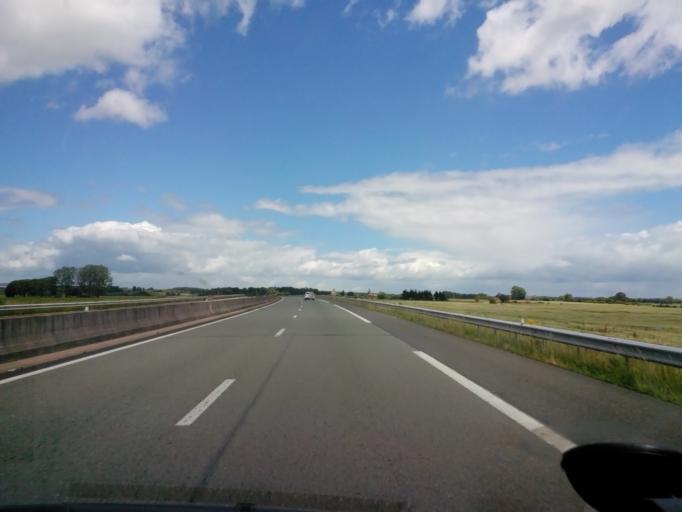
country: FR
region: Champagne-Ardenne
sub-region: Departement de la Haute-Marne
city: Saulxures
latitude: 48.0867
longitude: 5.6340
